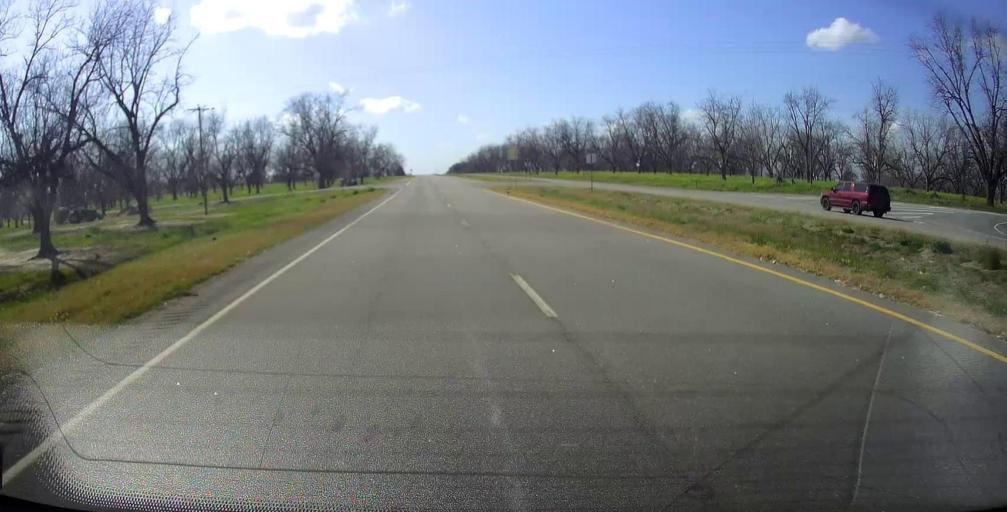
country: US
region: Georgia
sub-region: Dodge County
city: Eastman
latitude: 32.1985
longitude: -83.2267
